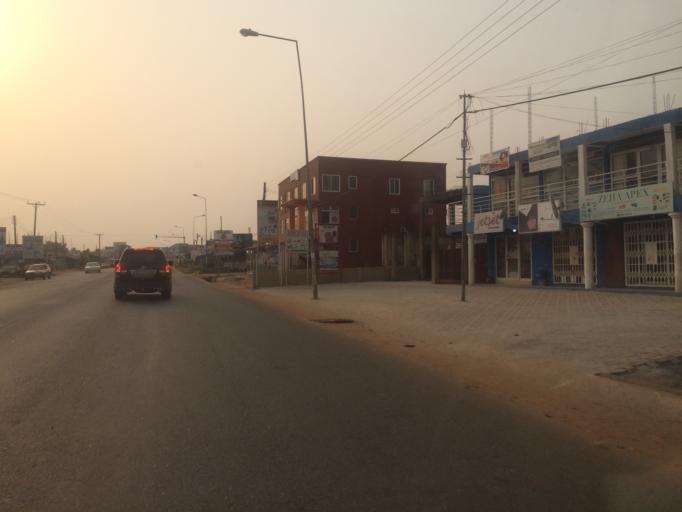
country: GH
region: Greater Accra
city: Nungua
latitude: 5.6387
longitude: -0.1058
